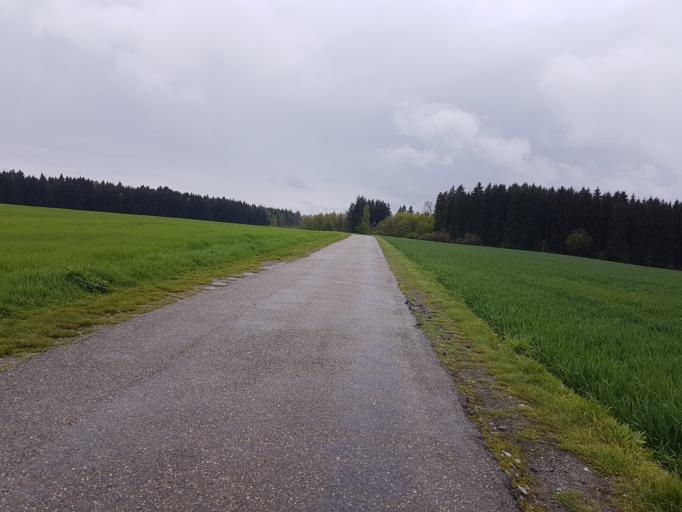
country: DE
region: Baden-Wuerttemberg
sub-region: Freiburg Region
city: Rottweil
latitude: 48.1886
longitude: 8.6168
